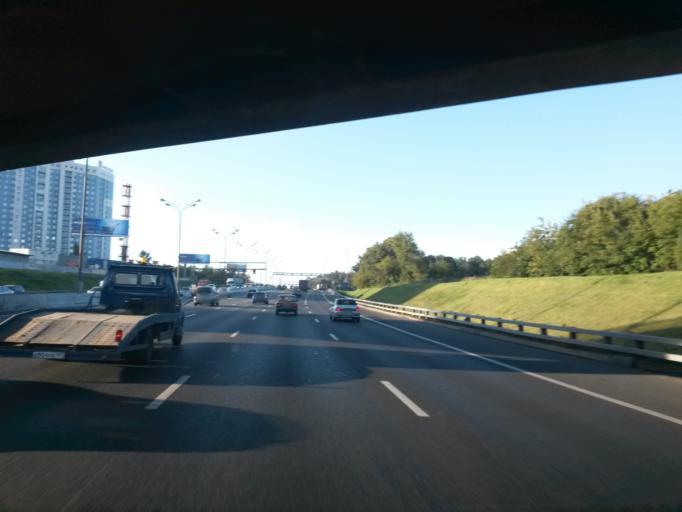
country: RU
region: Moscow
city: Vostochnyy
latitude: 55.8076
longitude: 37.8394
